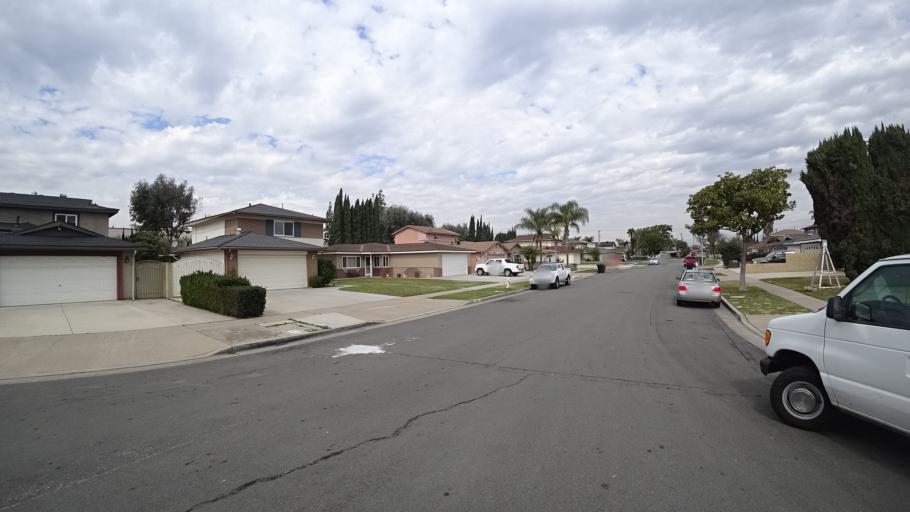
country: US
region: California
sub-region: Orange County
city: Anaheim
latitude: 33.8313
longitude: -117.8876
